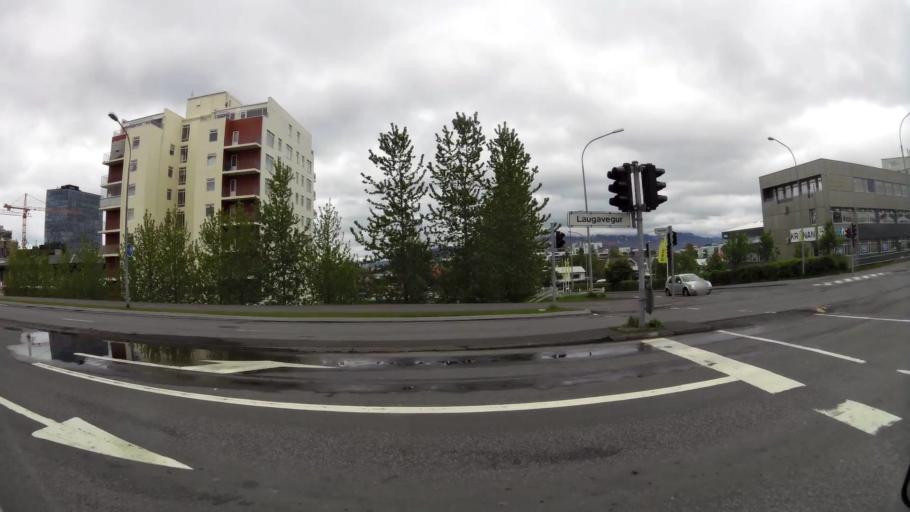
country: IS
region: Capital Region
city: Reykjavik
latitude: 64.1423
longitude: -21.9042
